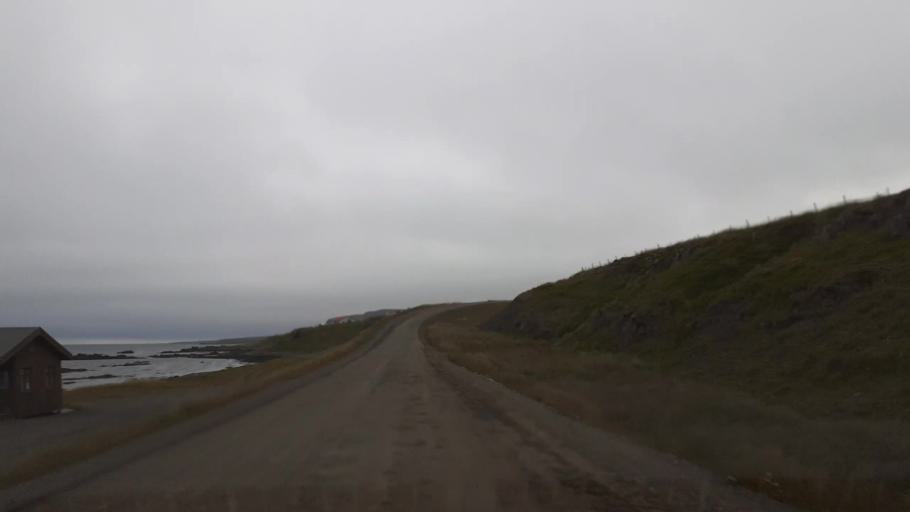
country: IS
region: Northwest
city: Saudarkrokur
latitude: 65.5283
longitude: -20.9615
